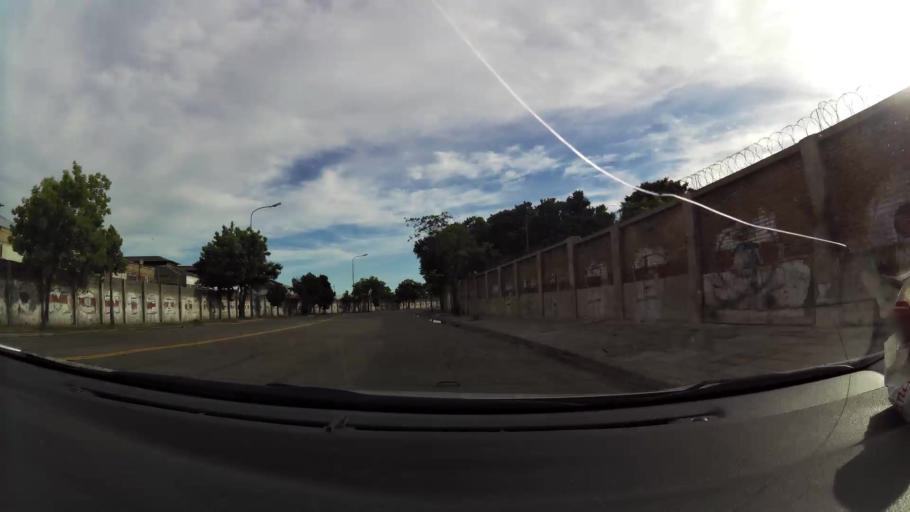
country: AR
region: Buenos Aires F.D.
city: Villa Lugano
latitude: -34.6486
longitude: -58.4504
